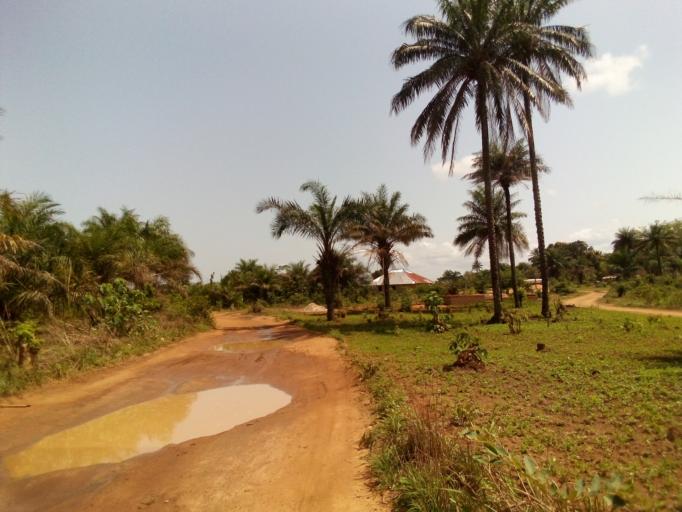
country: SL
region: Western Area
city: Waterloo
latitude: 8.3437
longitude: -13.0123
